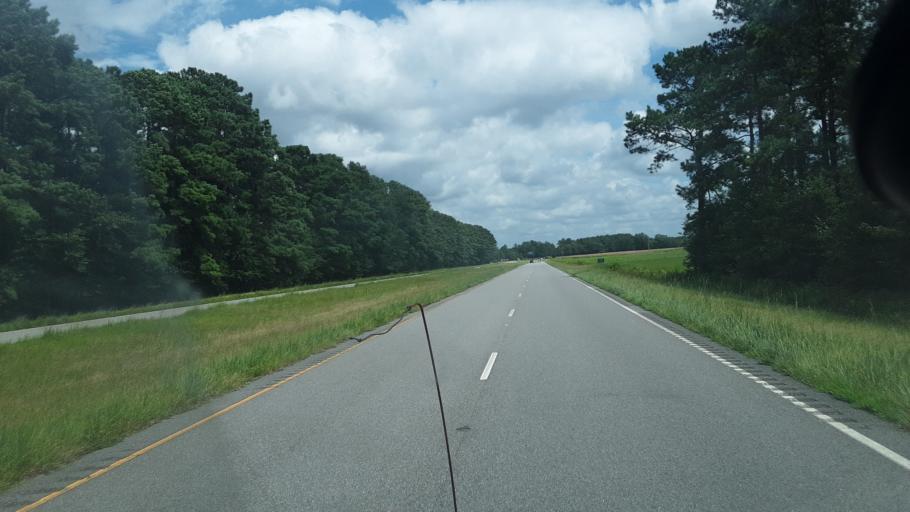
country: US
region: South Carolina
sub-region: Horry County
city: Loris
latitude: 34.1092
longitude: -78.9464
